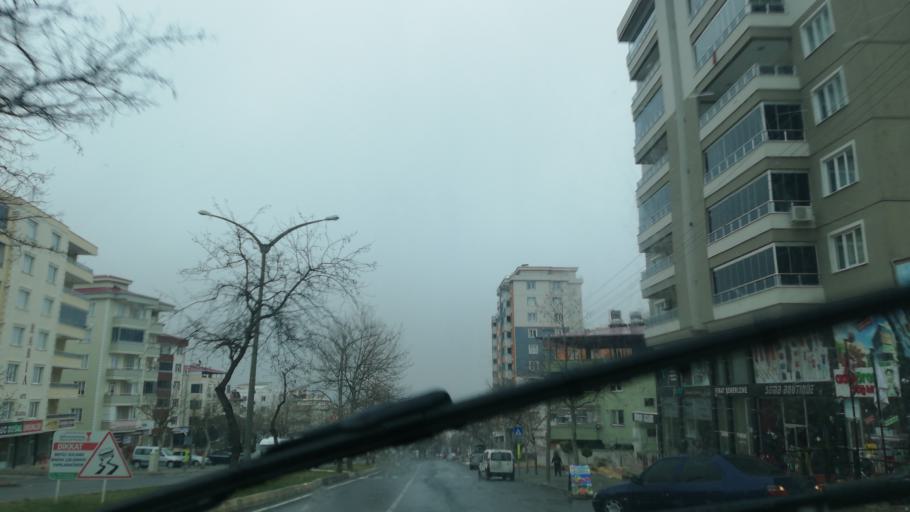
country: TR
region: Kahramanmaras
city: Kahramanmaras
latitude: 37.5920
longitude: 36.8998
